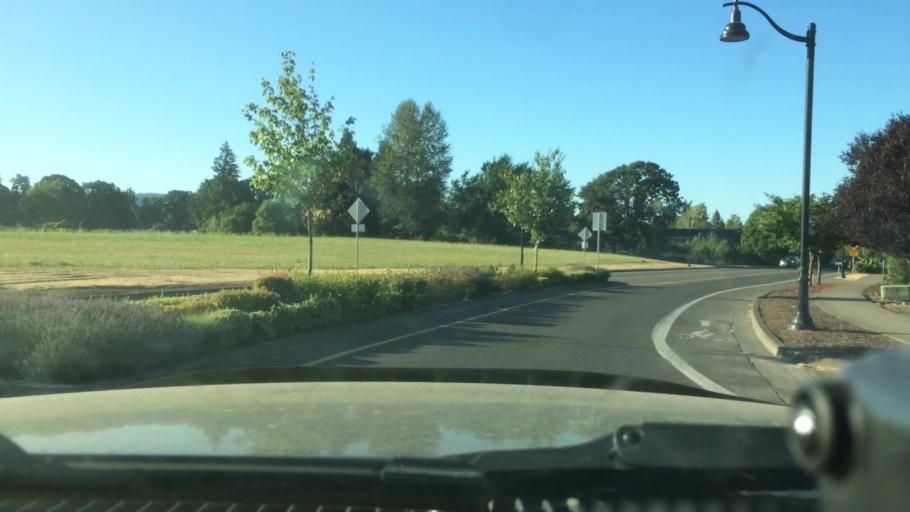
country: US
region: Oregon
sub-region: Yamhill County
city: Newberg
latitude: 45.3150
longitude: -122.9459
